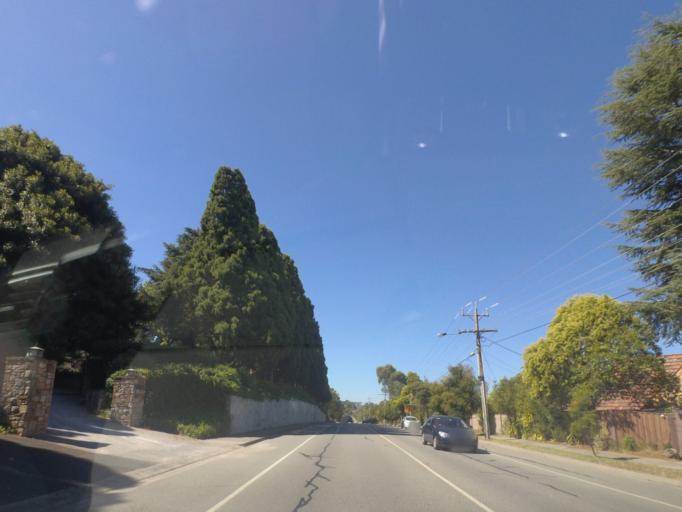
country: AU
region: Victoria
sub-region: Maroondah
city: Warranwood
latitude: -37.7933
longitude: 145.2433
